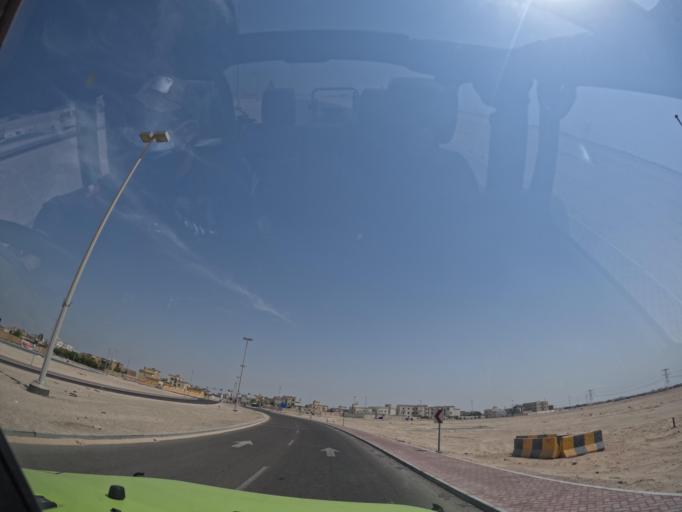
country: AE
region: Abu Dhabi
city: Abu Dhabi
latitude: 24.3052
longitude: 54.5490
